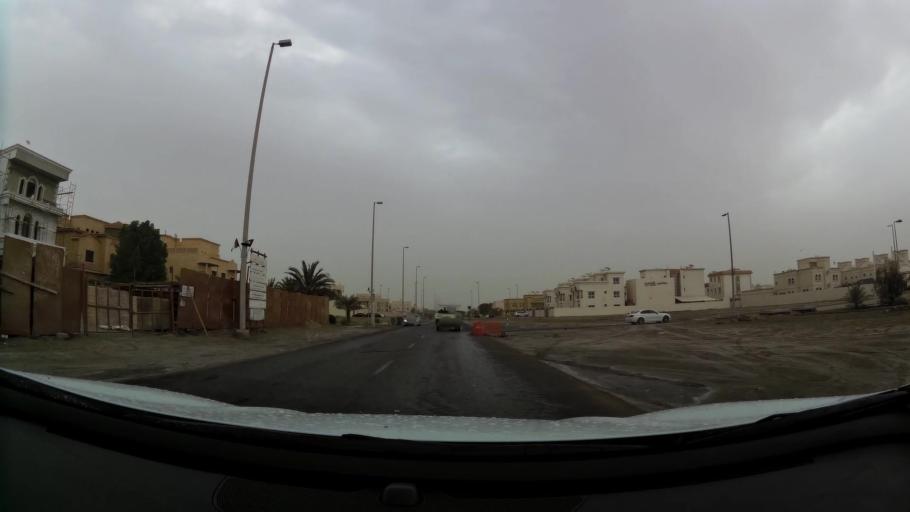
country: AE
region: Abu Dhabi
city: Abu Dhabi
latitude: 24.4115
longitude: 54.5866
